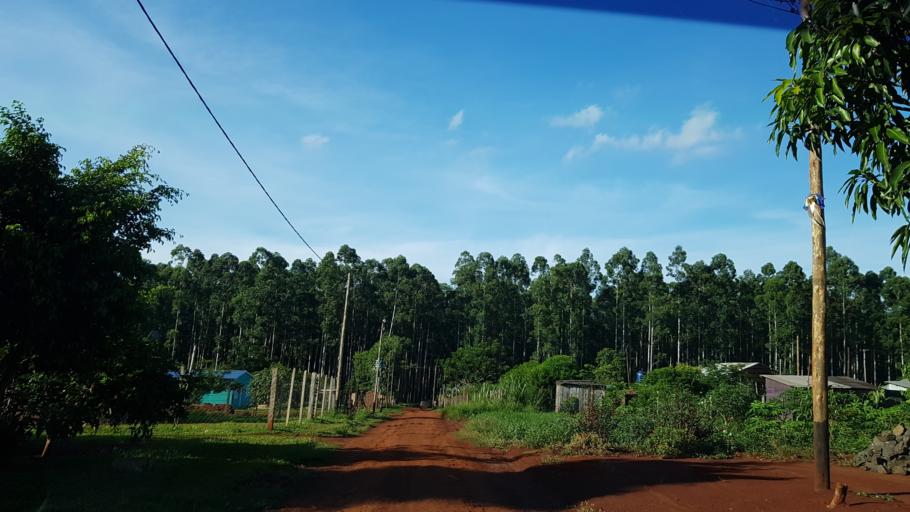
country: AR
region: Misiones
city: Puerto Libertad
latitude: -25.9153
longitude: -54.5905
